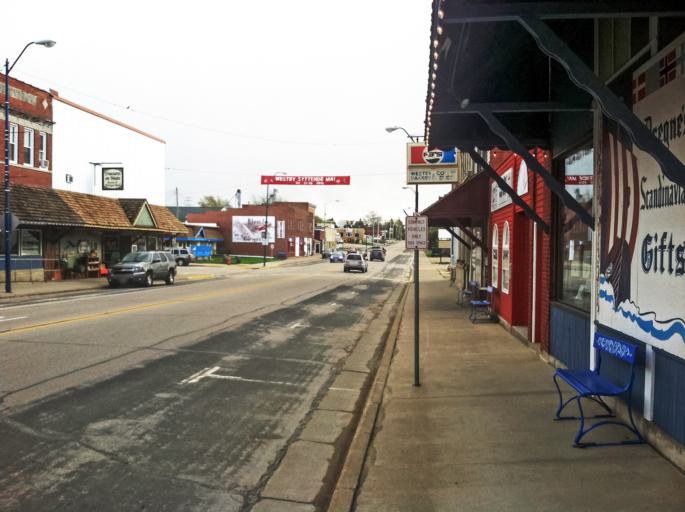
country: US
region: Wisconsin
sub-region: Vernon County
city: Westby
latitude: 43.6532
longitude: -90.8576
